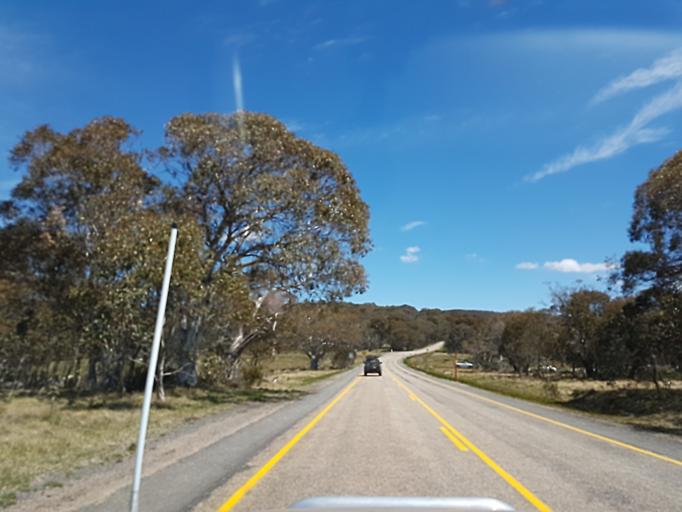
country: AU
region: Victoria
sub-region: Alpine
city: Mount Beauty
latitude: -37.0277
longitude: 147.2858
